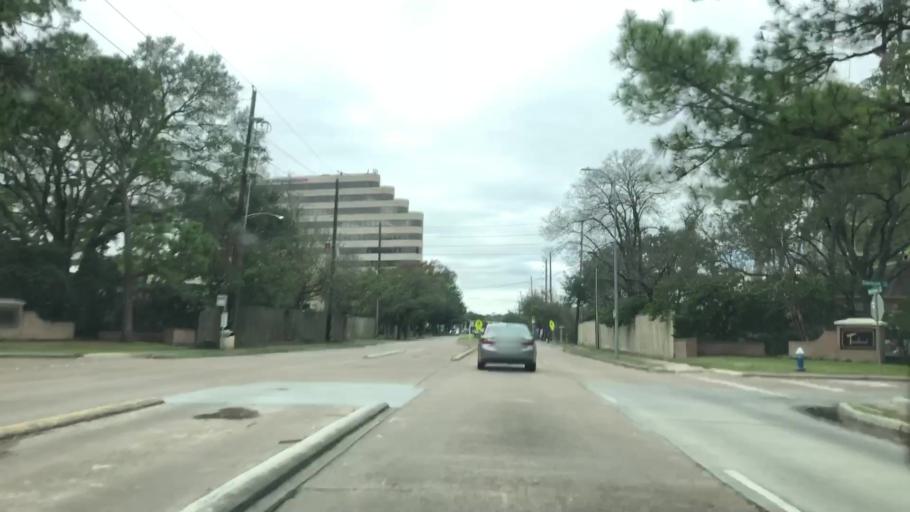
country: US
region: Texas
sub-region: Harris County
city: Hunters Creek Village
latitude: 29.7566
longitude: -95.4945
